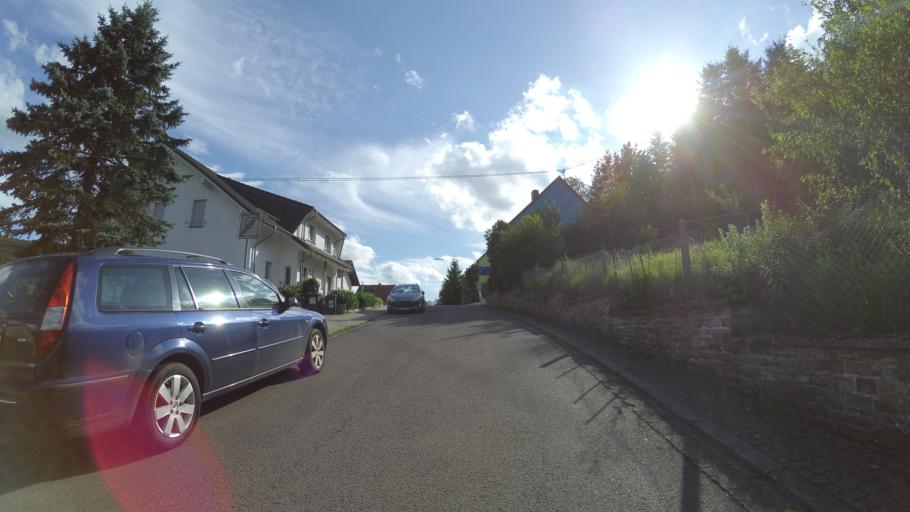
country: DE
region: Saarland
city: Nonnweiler
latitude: 49.5848
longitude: 6.9886
